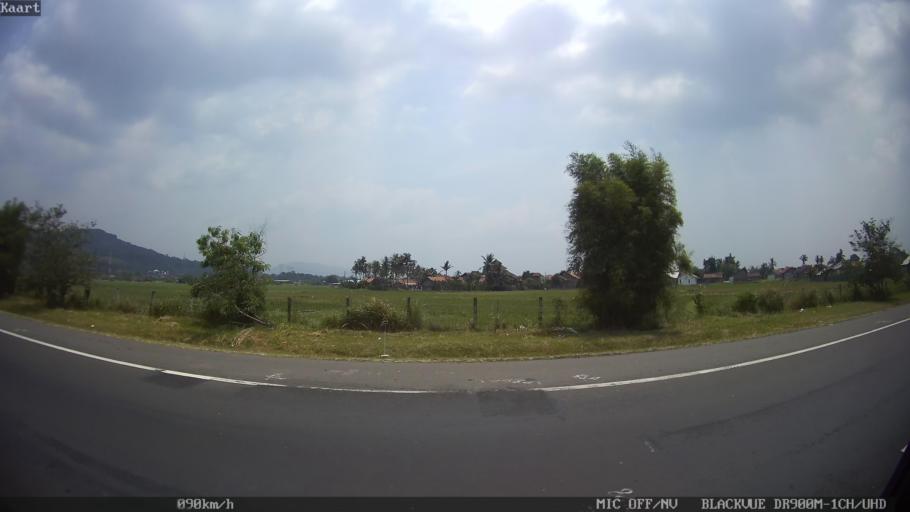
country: ID
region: Banten
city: Bojonegara
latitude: -6.0377
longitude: 106.1034
